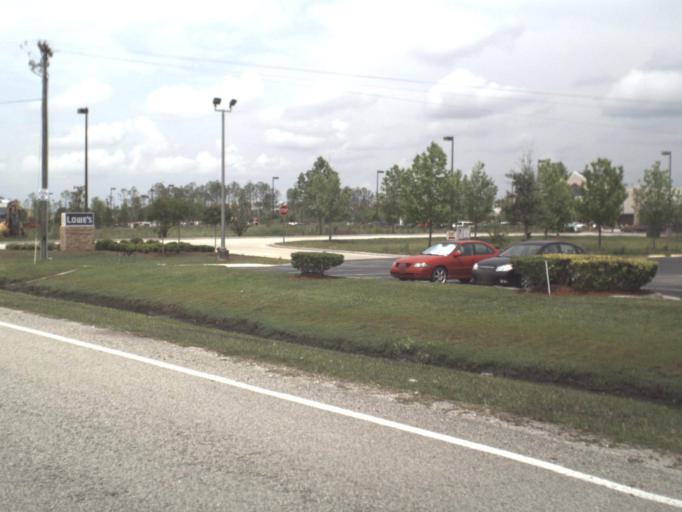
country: US
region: Florida
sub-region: Clay County
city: Middleburg
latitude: 30.1090
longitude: -81.8220
